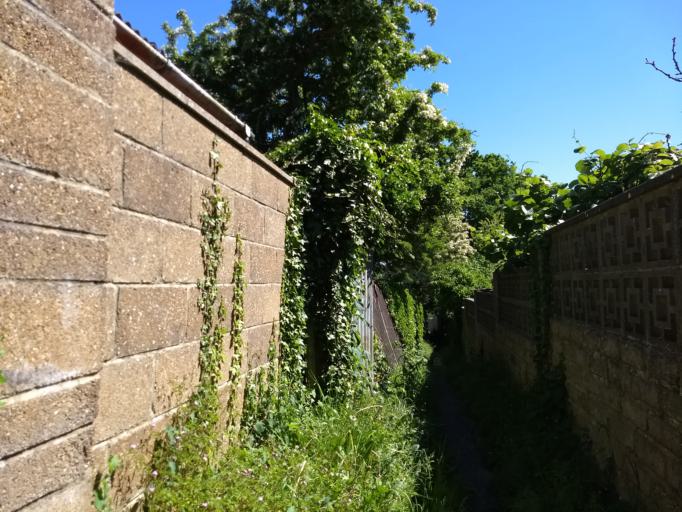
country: GB
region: England
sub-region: Isle of Wight
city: Seaview
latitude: 50.6957
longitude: -1.1098
